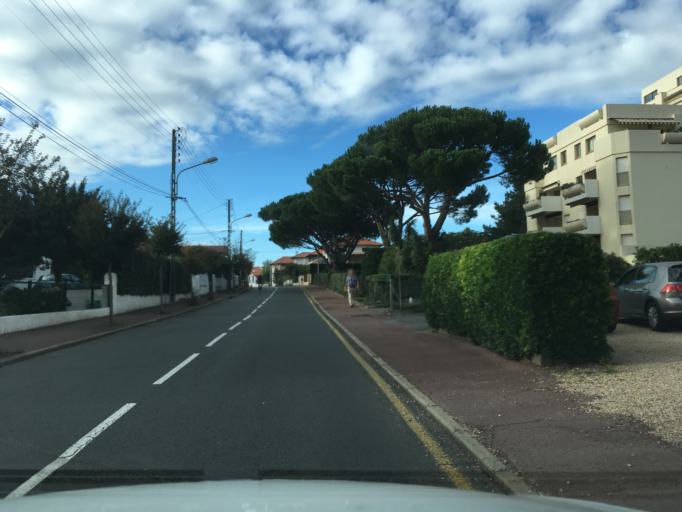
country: FR
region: Aquitaine
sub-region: Departement des Pyrenees-Atlantiques
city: Biarritz
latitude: 43.4892
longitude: -1.5440
